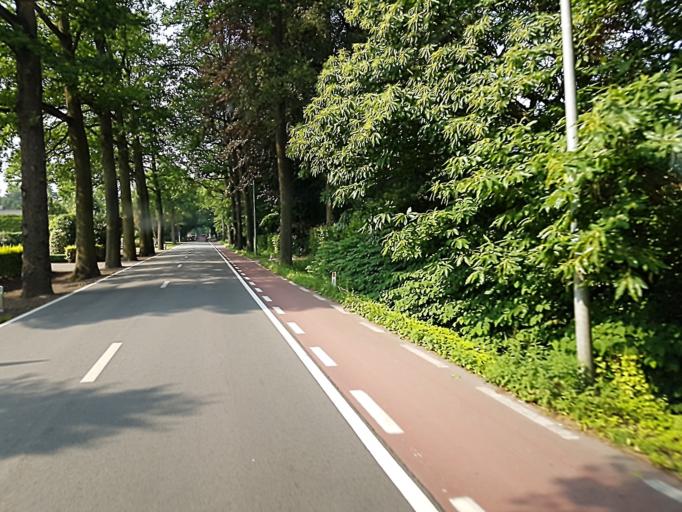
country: BE
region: Flanders
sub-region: Provincie Antwerpen
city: Turnhout
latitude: 51.3403
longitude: 4.9446
